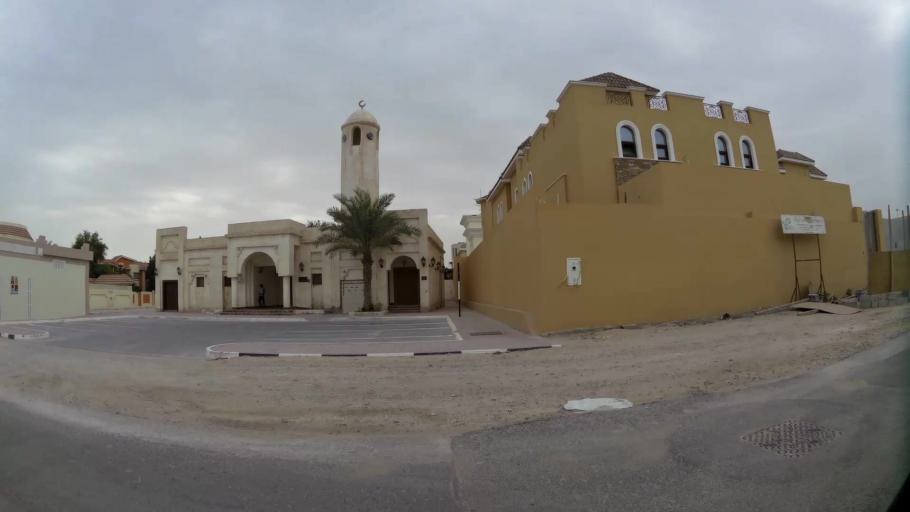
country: QA
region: Baladiyat ar Rayyan
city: Ar Rayyan
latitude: 25.3456
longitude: 51.4663
